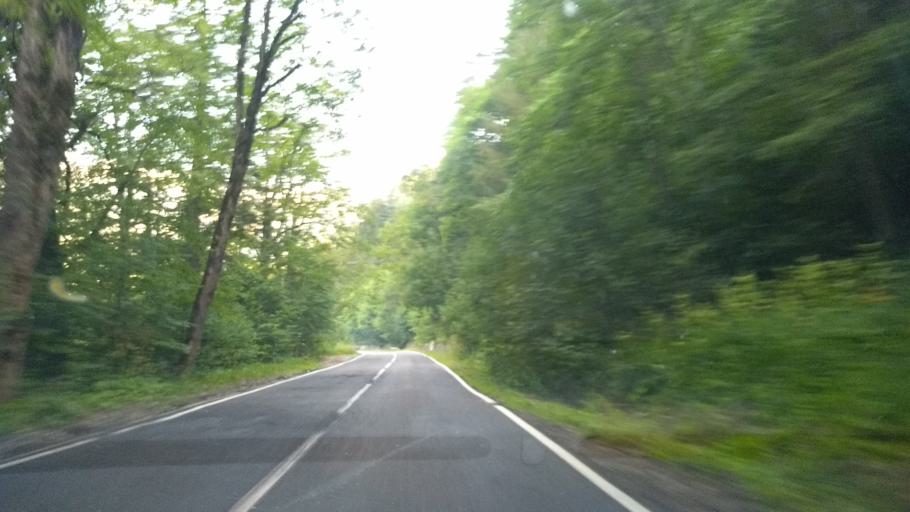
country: RO
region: Prahova
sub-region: Oras Sinaia
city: Sinaia
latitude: 45.3268
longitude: 25.5253
